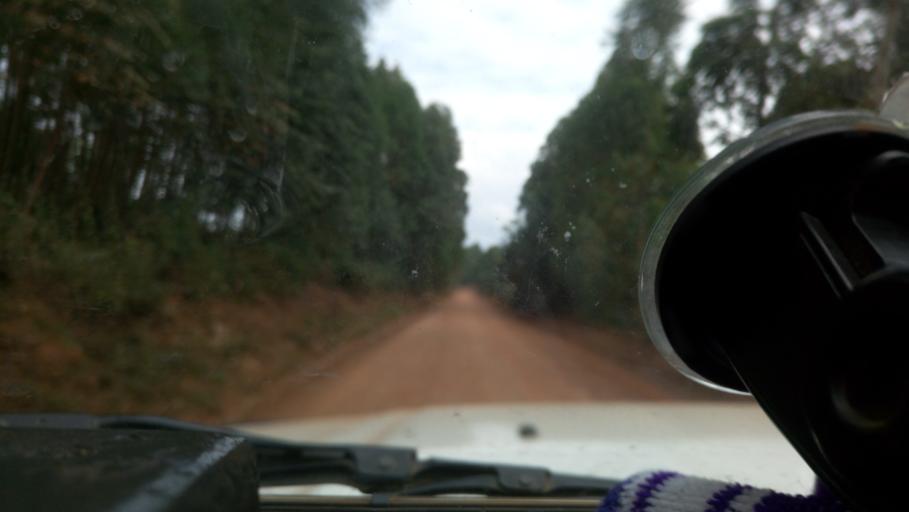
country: KE
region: Kericho
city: Litein
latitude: -0.6009
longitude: 35.1806
